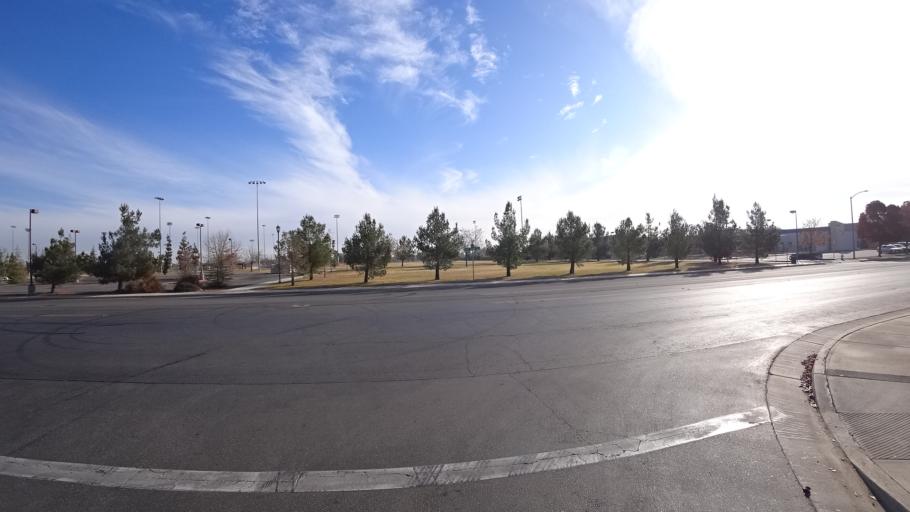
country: US
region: California
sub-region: Kern County
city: Rosedale
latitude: 35.4020
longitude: -119.1369
